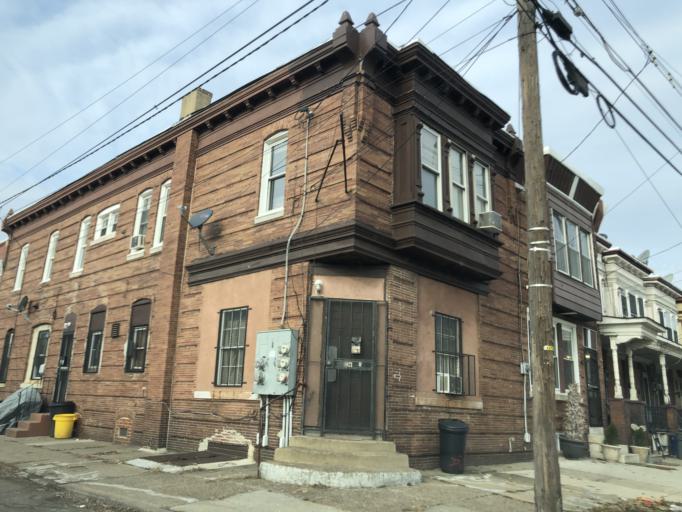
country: US
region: New Jersey
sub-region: Camden County
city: Camden
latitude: 39.9202
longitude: -75.1215
